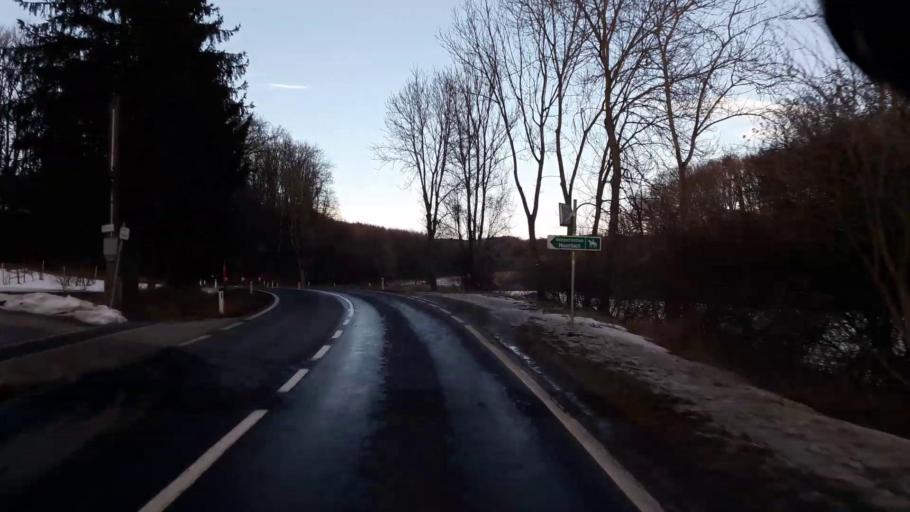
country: AT
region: Lower Austria
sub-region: Politischer Bezirk Wien-Umgebung
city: Mauerbach
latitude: 48.2536
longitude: 16.1651
